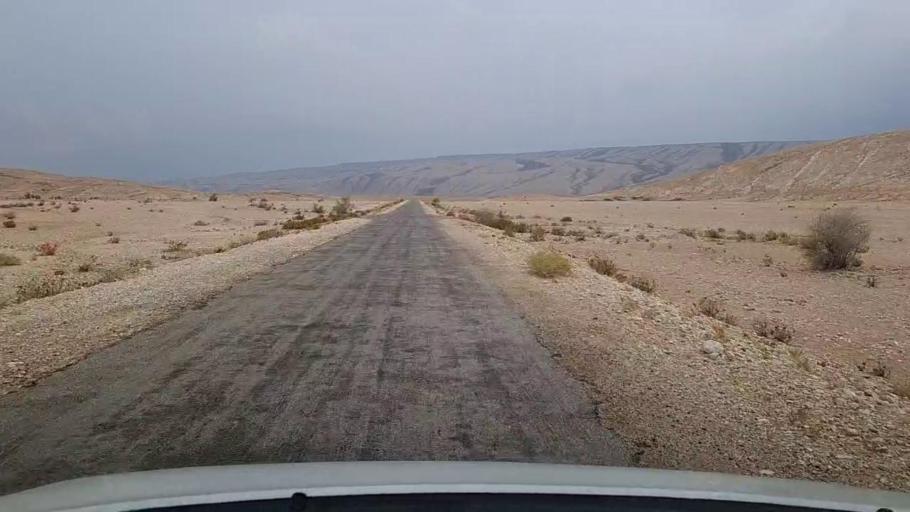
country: PK
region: Sindh
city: Sehwan
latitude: 26.2331
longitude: 67.7091
